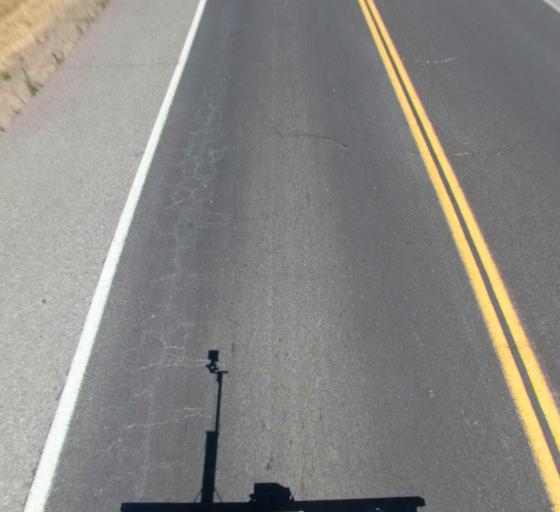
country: US
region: California
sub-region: Madera County
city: Parkwood
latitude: 36.9237
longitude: -120.0639
